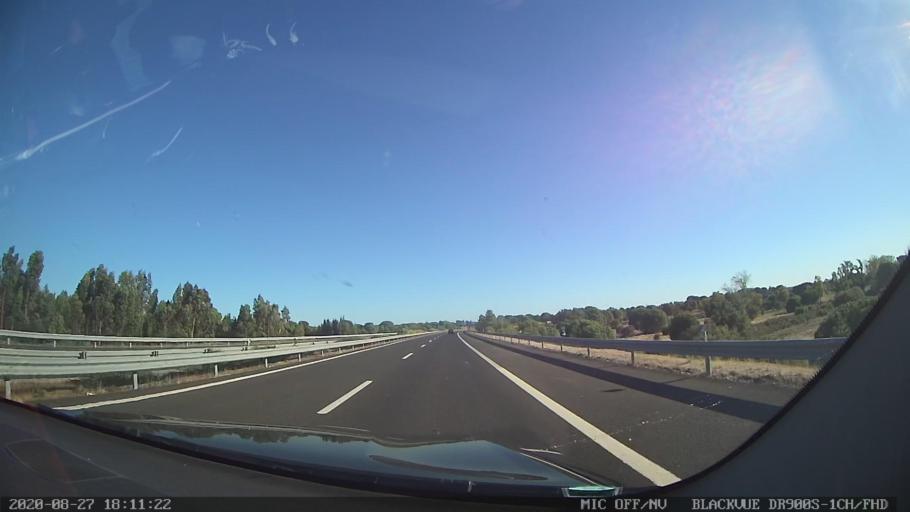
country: PT
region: Evora
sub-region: Vendas Novas
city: Vendas Novas
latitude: 38.6946
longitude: -8.6395
